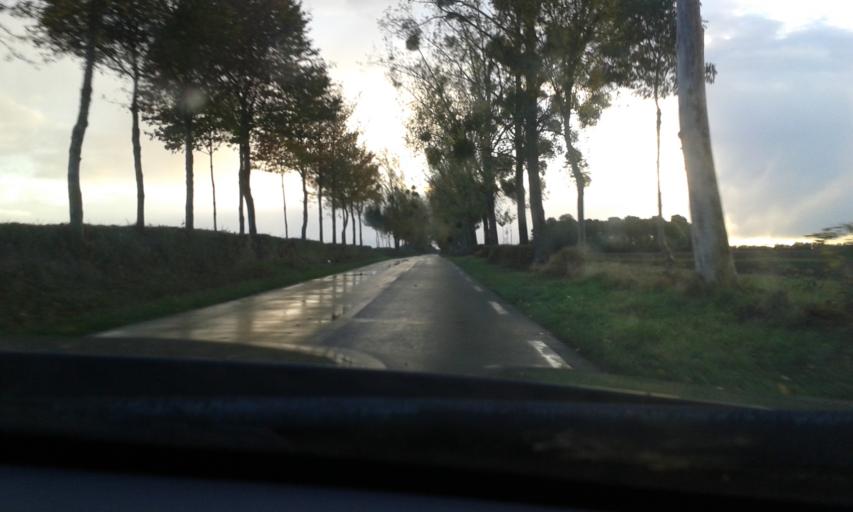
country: FR
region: Centre
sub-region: Departement du Loiret
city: Chevilly
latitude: 48.0213
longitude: 1.8565
